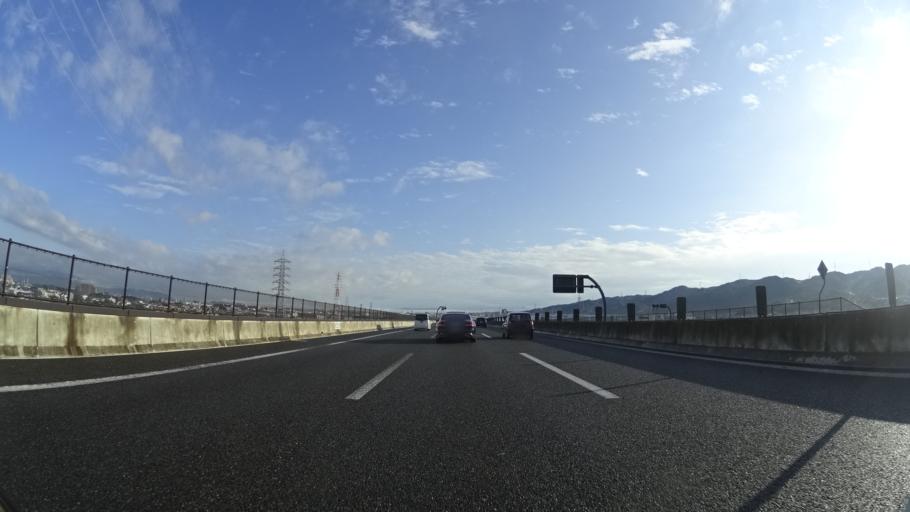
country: JP
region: Osaka
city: Neyagawa
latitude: 34.7762
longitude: 135.6652
